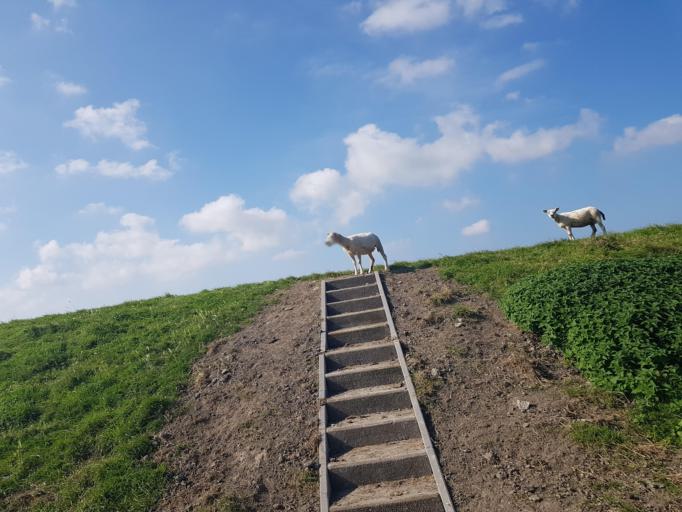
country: NL
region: North Holland
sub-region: Gemeente Texel
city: Den Burg
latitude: 53.1043
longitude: 4.8579
